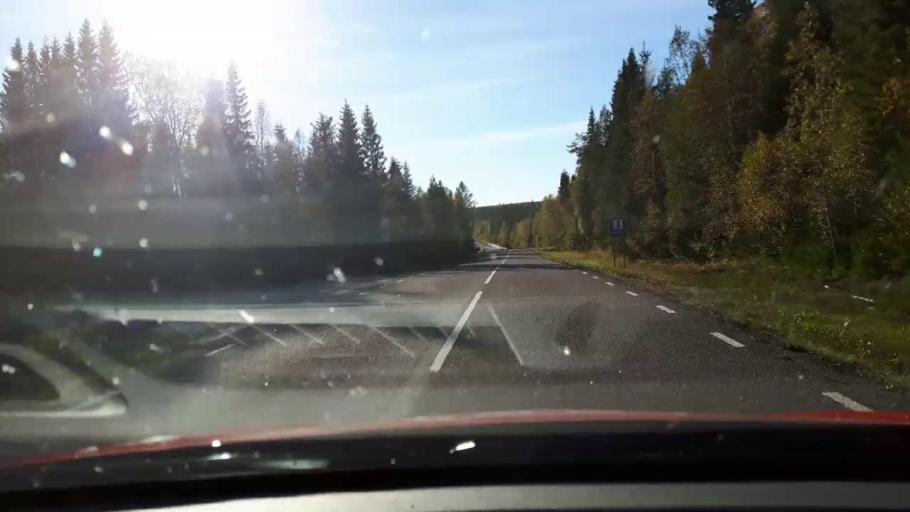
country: SE
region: Jaemtland
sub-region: Stroemsunds Kommun
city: Stroemsund
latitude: 63.8670
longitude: 15.1095
